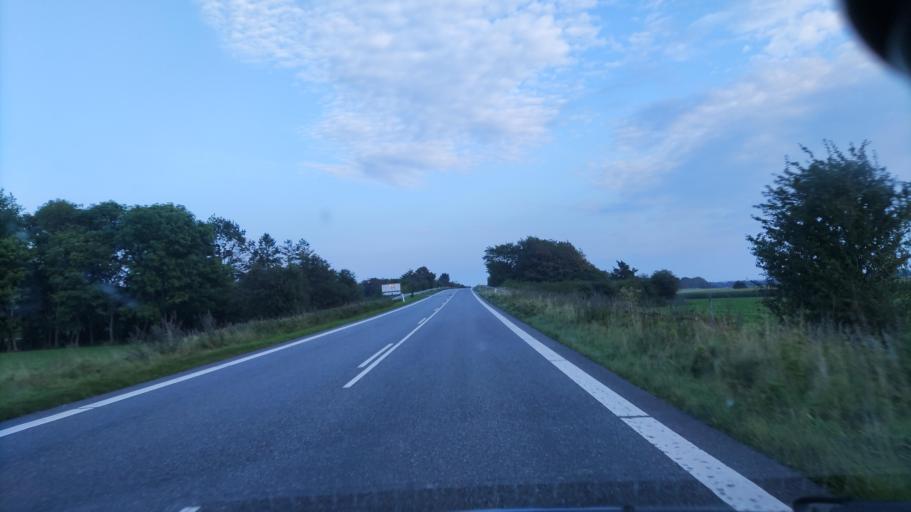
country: DK
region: South Denmark
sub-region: Aabenraa Kommune
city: Tinglev
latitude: 54.8768
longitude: 9.3017
